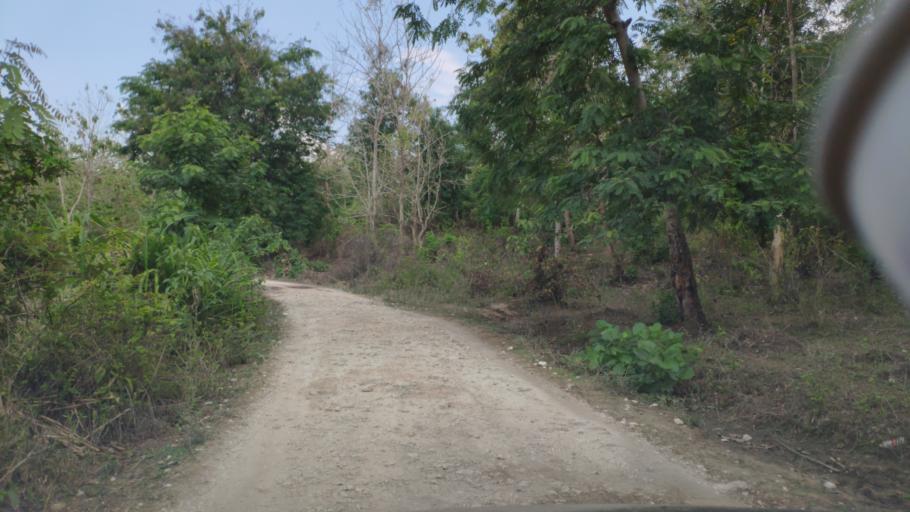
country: ID
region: Central Java
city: Semanggi
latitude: -7.0572
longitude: 111.4208
